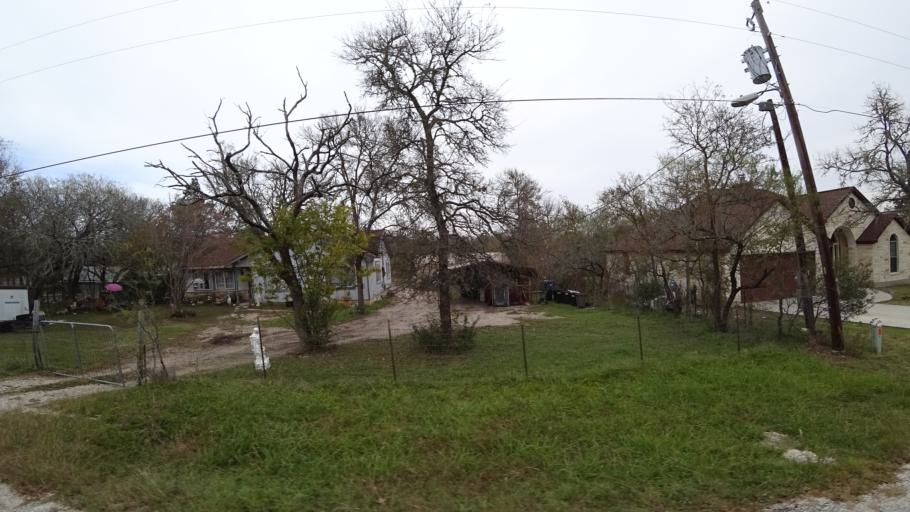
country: US
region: Texas
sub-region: Travis County
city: Garfield
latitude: 30.1011
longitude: -97.5715
